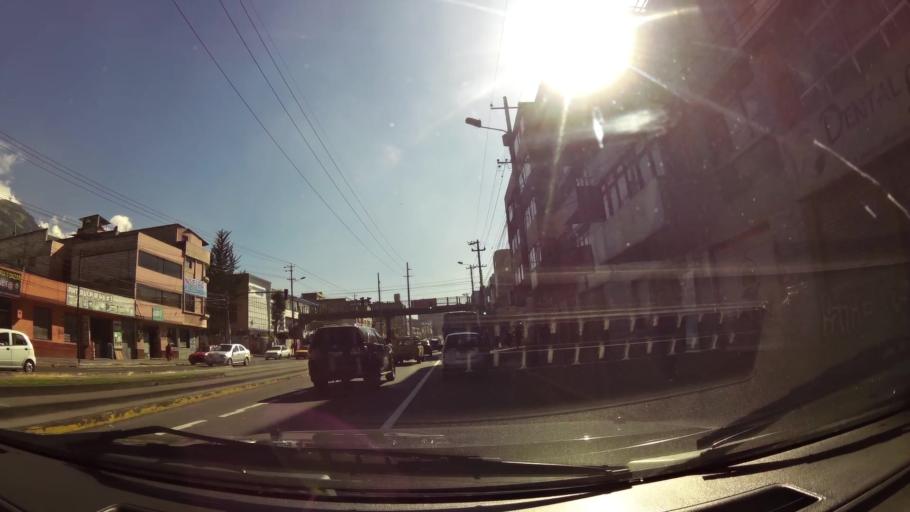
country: EC
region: Pichincha
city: Quito
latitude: -0.2406
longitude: -78.5314
